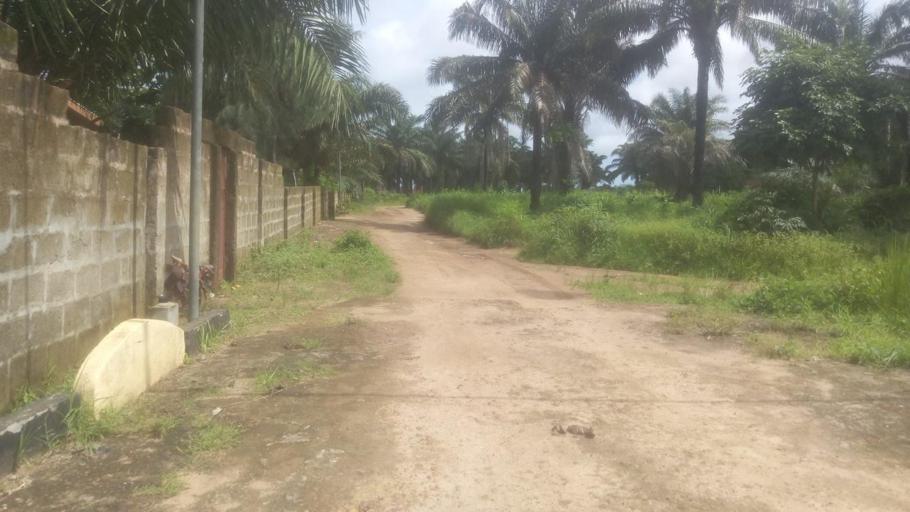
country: SL
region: Northern Province
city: Masoyila
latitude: 8.5952
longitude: -13.1876
